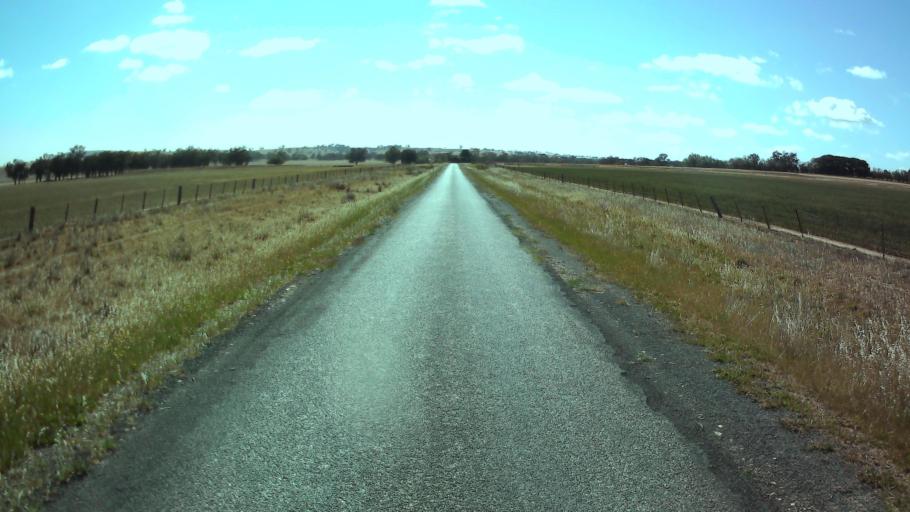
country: AU
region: New South Wales
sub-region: Young
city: Young
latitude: -34.0756
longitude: 148.3576
